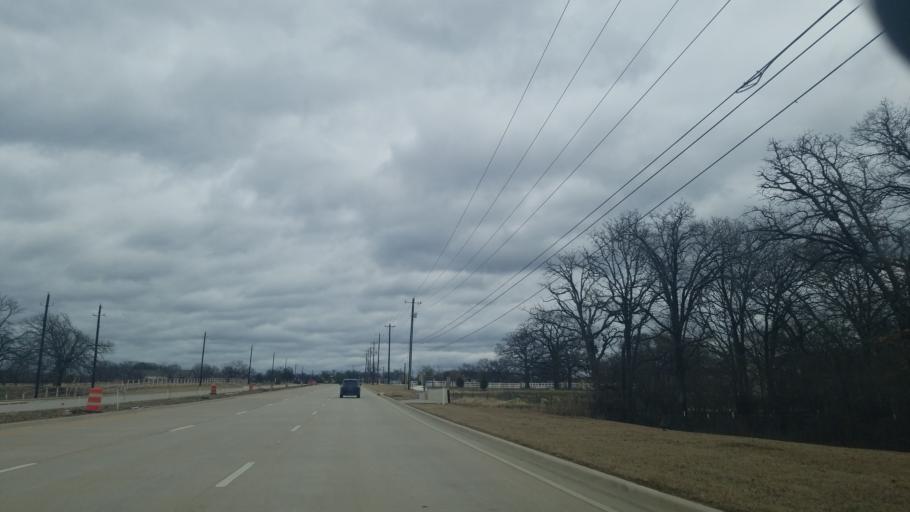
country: US
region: Texas
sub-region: Denton County
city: Bartonville
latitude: 33.0472
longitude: -97.1355
